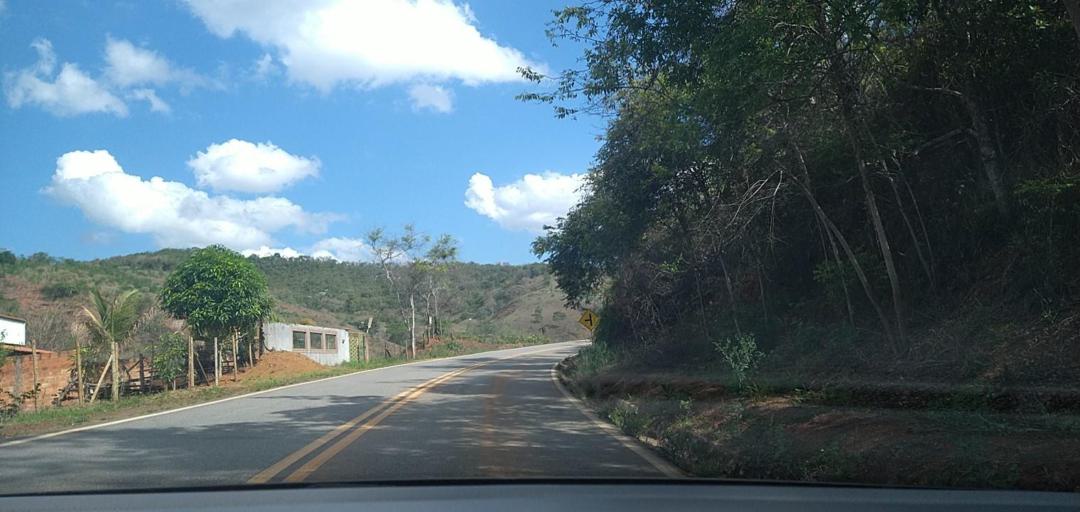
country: BR
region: Minas Gerais
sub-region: Rio Piracicaba
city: Rio Piracicaba
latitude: -20.0062
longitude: -43.0969
